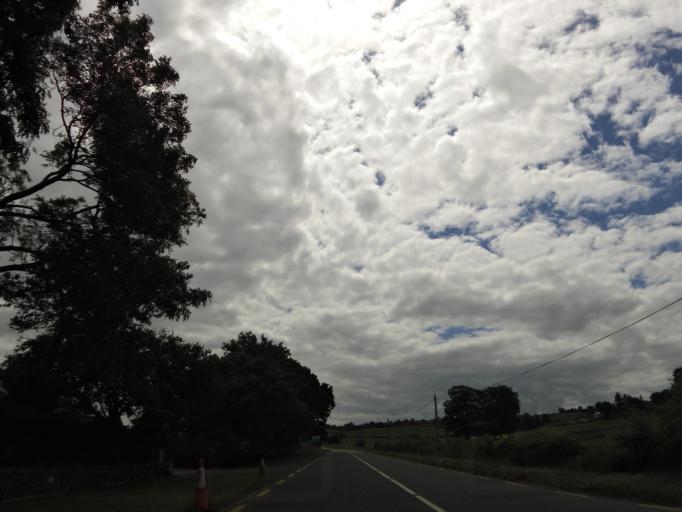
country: IE
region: Munster
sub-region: North Tipperary
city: Nenagh
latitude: 52.7750
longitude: -8.0285
